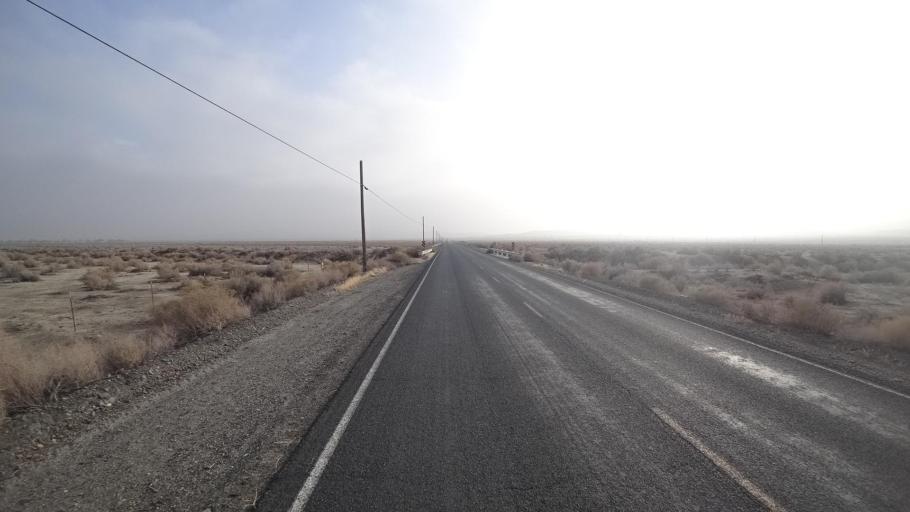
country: US
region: California
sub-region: Kern County
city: Ford City
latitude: 35.2232
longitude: -119.4456
